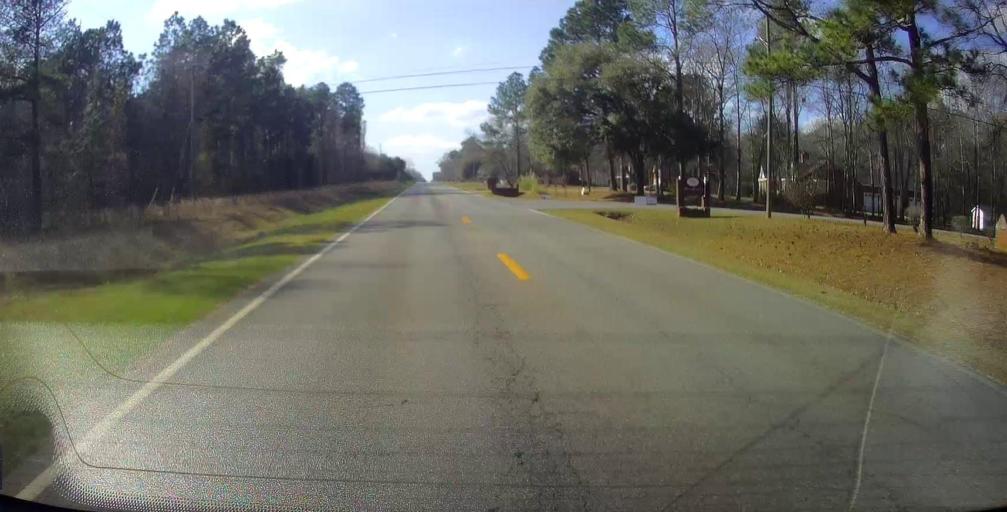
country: US
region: Georgia
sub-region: Laurens County
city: Dublin
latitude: 32.5586
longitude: -83.0043
